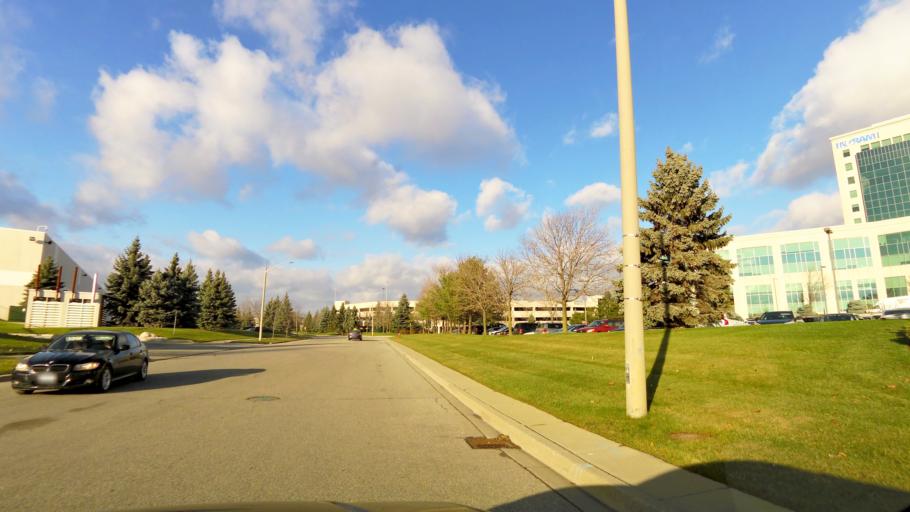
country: CA
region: Ontario
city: Mississauga
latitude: 43.6248
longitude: -79.6864
